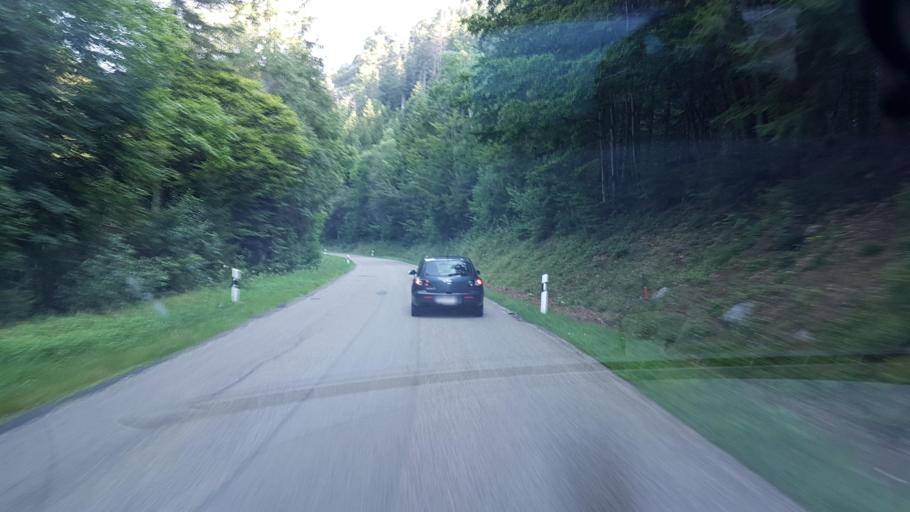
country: DE
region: Baden-Wuerttemberg
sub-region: Freiburg Region
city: Hochenschwand
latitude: 47.7301
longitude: 8.1450
